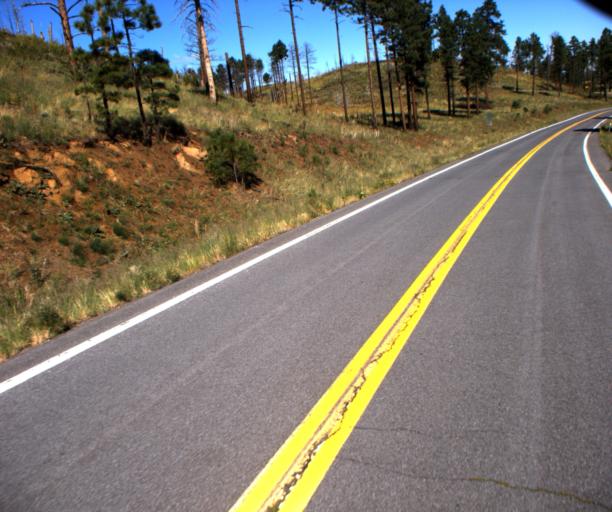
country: US
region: Arizona
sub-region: Apache County
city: Eagar
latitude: 34.0568
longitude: -109.3566
